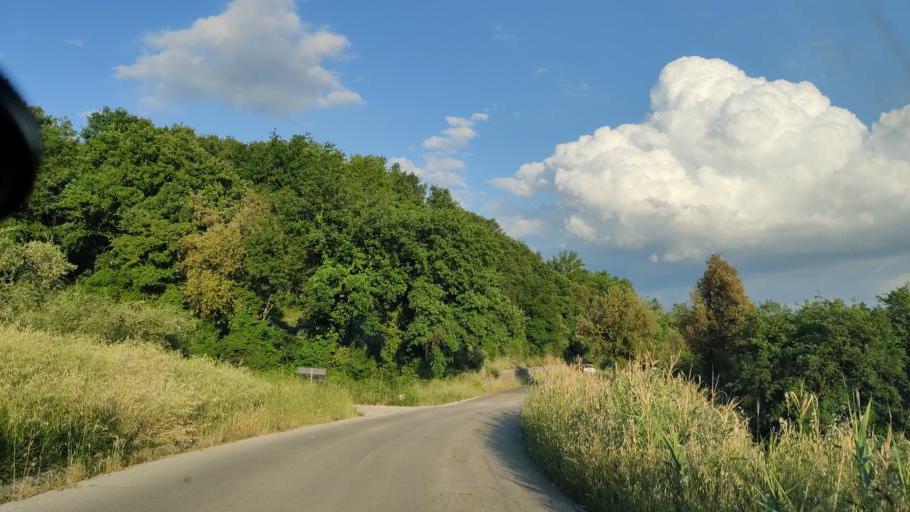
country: IT
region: Umbria
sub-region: Provincia di Terni
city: Amelia
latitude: 42.5802
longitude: 12.3912
